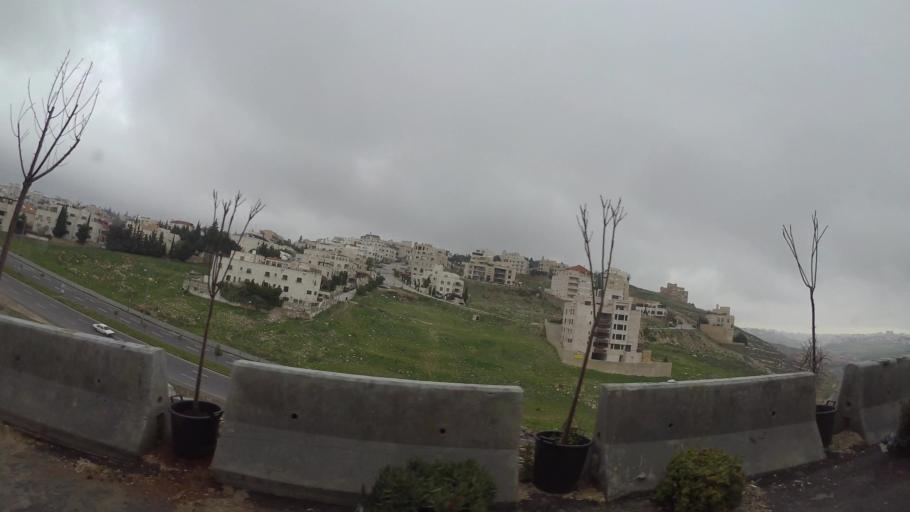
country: JO
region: Amman
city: Wadi as Sir
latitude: 31.9397
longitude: 35.8693
